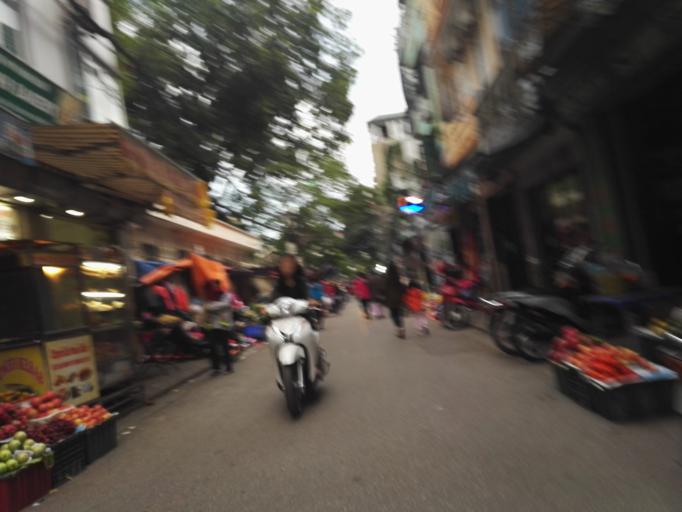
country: VN
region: Ha Noi
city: Hoan Kiem
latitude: 21.0442
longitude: 105.8502
